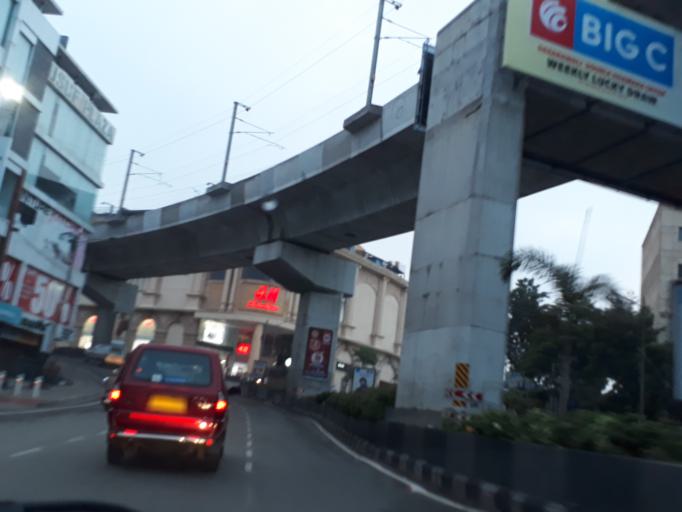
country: IN
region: Telangana
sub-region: Rangareddi
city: Kukatpalli
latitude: 17.4320
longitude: 78.4070
